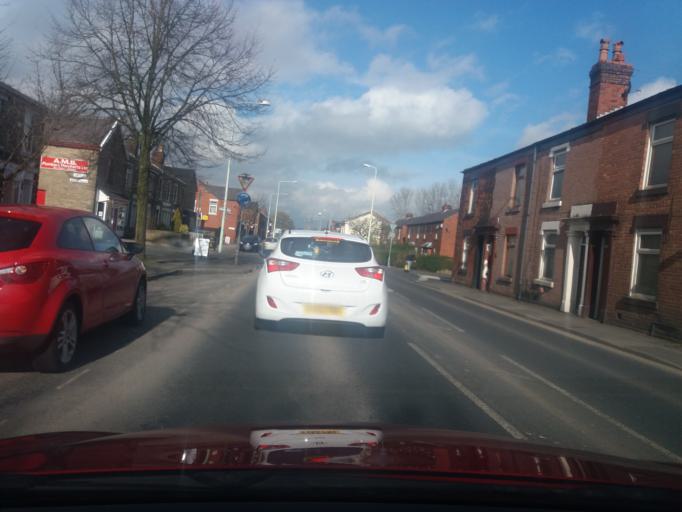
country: GB
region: England
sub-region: Lancashire
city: Chorley
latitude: 53.6453
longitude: -2.6360
